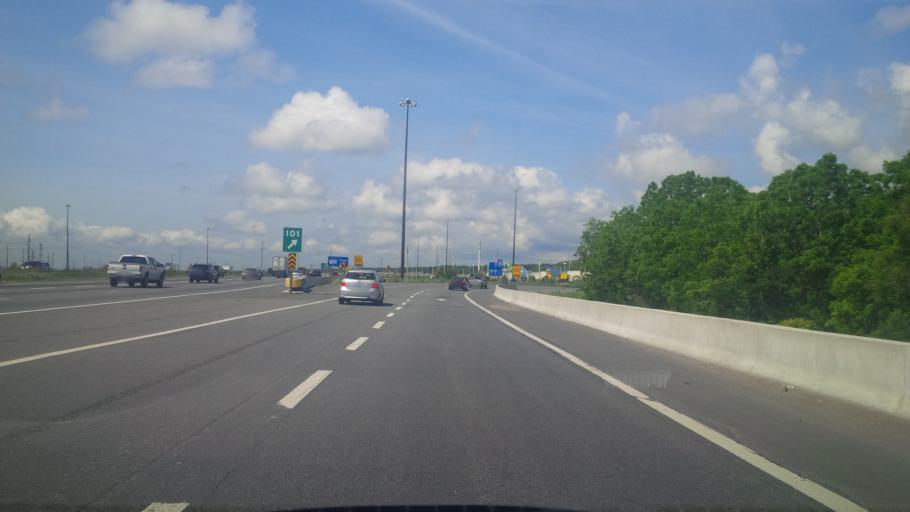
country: CA
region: Ontario
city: Burlington
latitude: 43.3436
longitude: -79.8192
